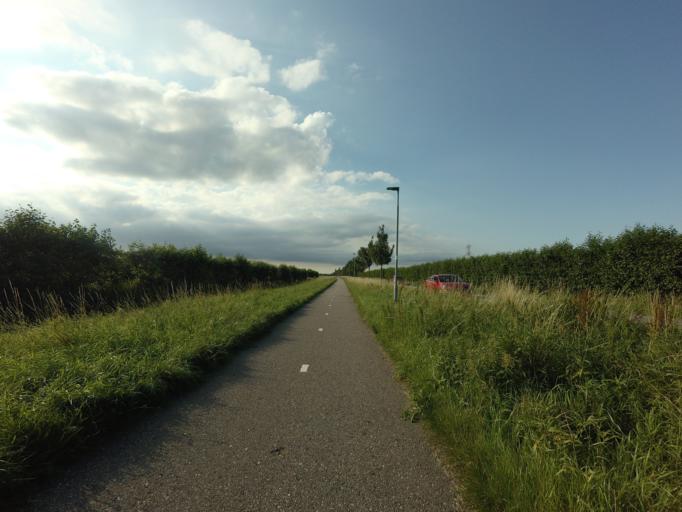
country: NL
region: North Holland
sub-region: Gemeente Hoorn
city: Hoorn
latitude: 52.6864
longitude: 5.0820
